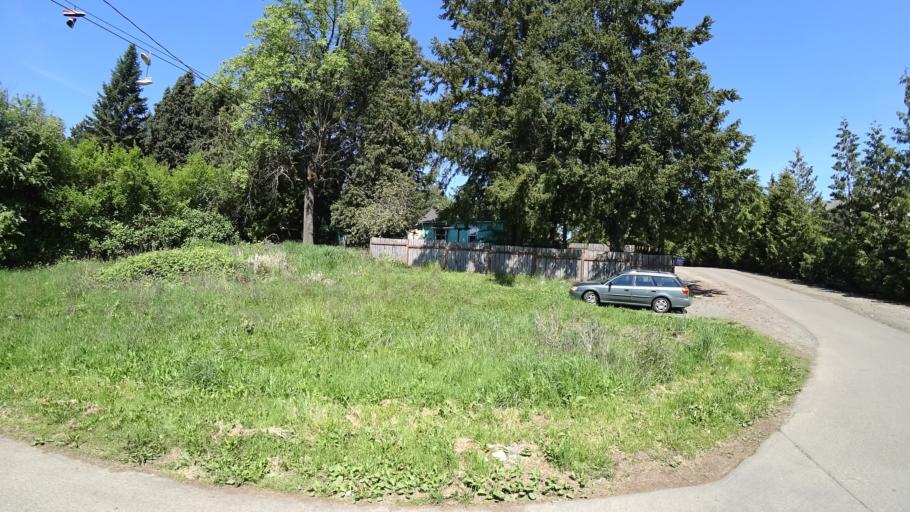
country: US
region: Oregon
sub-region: Washington County
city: Hillsboro
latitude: 45.5111
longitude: -122.9768
